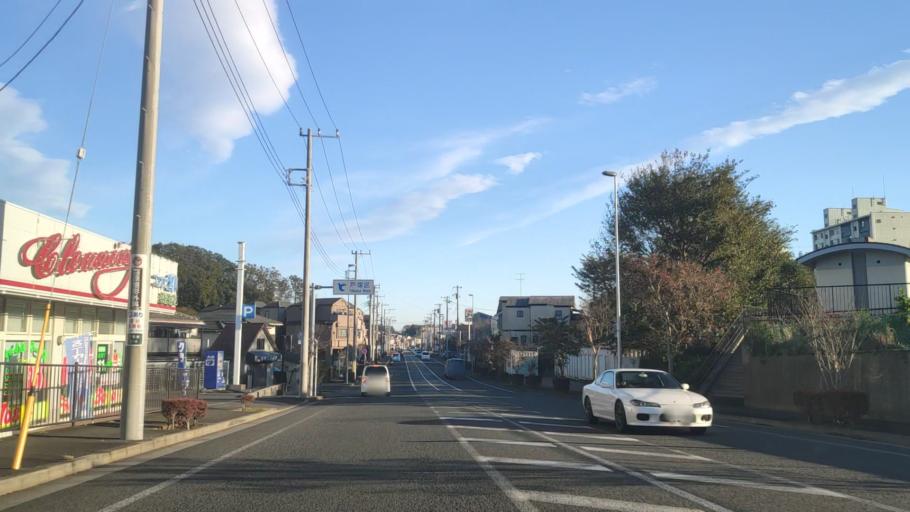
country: JP
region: Kanagawa
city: Fujisawa
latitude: 35.3921
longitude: 139.4926
